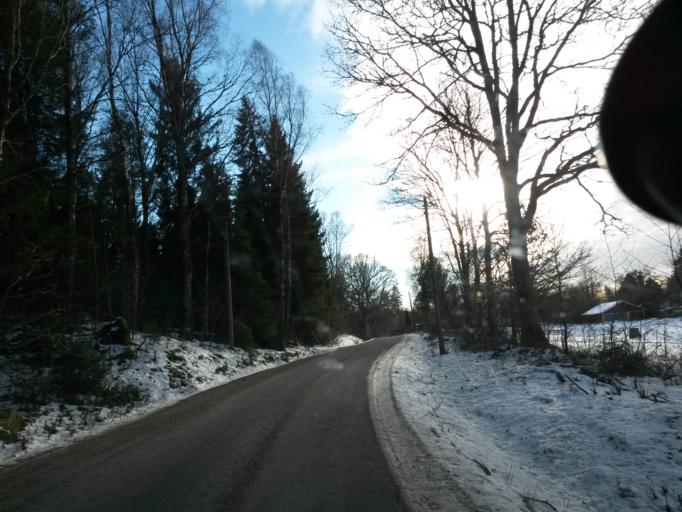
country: SE
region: Vaestra Goetaland
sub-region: Vargarda Kommun
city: Vargarda
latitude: 58.0114
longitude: 12.8918
